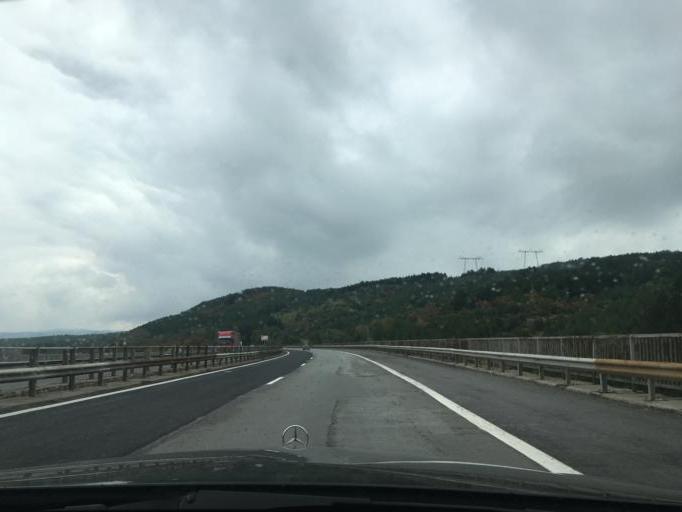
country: BG
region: Sofiya
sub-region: Obshtina Elin Pelin
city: Elin Pelin
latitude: 42.5952
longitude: 23.5901
